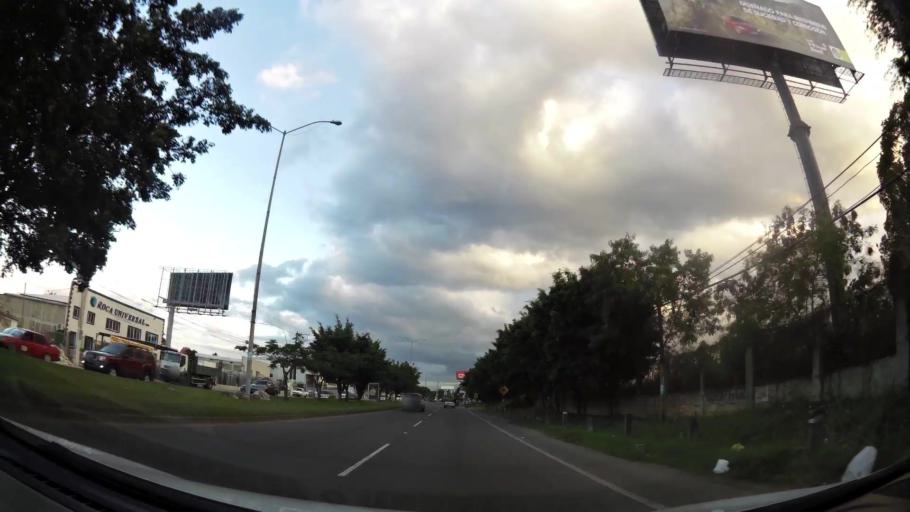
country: DO
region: Santiago
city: Licey al Medio
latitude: 19.4071
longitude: -70.6378
